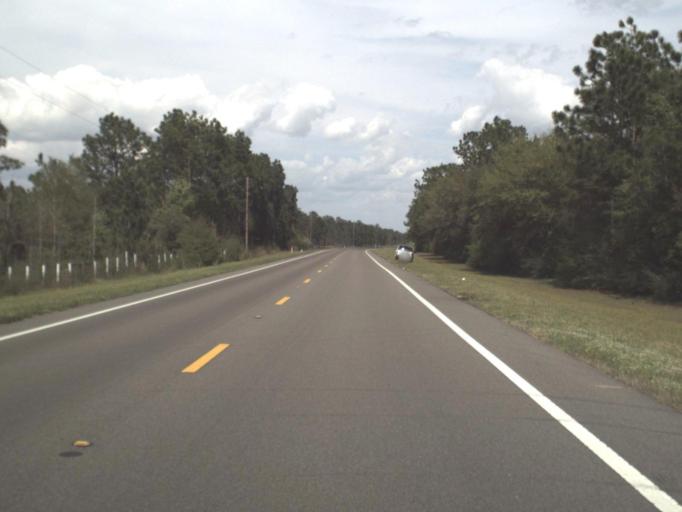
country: US
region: Florida
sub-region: Santa Rosa County
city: East Milton
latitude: 30.6825
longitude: -86.8352
